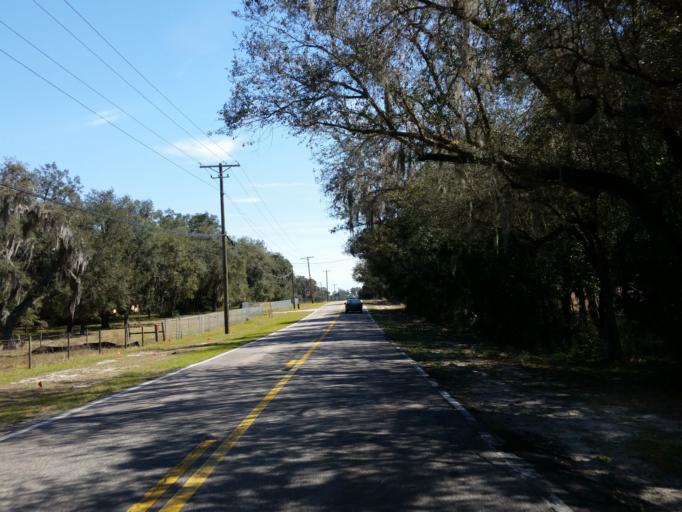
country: US
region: Florida
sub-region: Hillsborough County
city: Boyette
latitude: 27.8355
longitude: -82.2532
